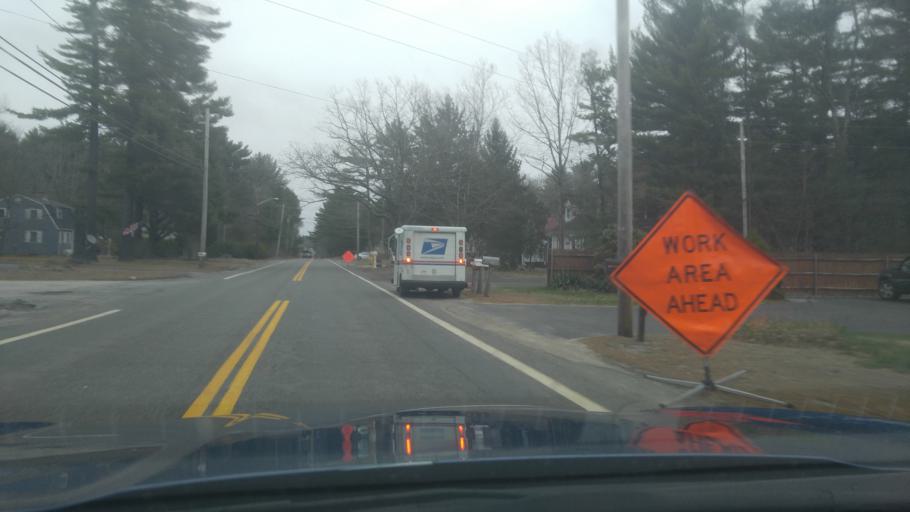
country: US
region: Rhode Island
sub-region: Kent County
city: West Greenwich
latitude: 41.6673
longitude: -71.6114
